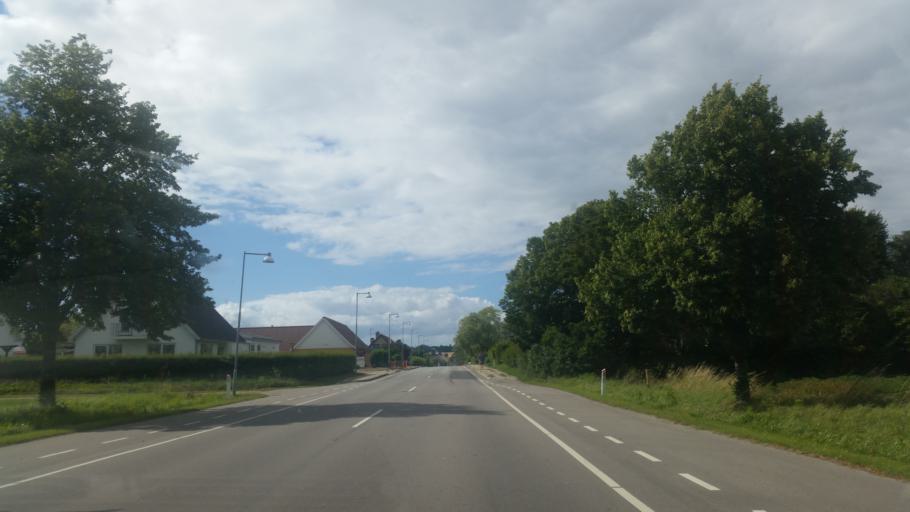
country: DK
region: Zealand
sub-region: Odsherred Kommune
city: Horve
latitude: 55.7994
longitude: 11.4465
